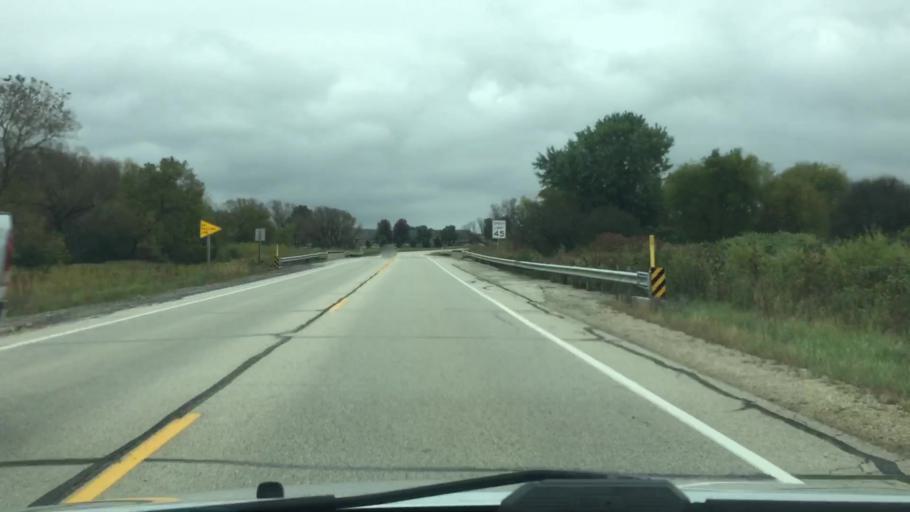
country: US
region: Wisconsin
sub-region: Walworth County
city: Elkhorn
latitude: 42.7352
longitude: -88.5460
